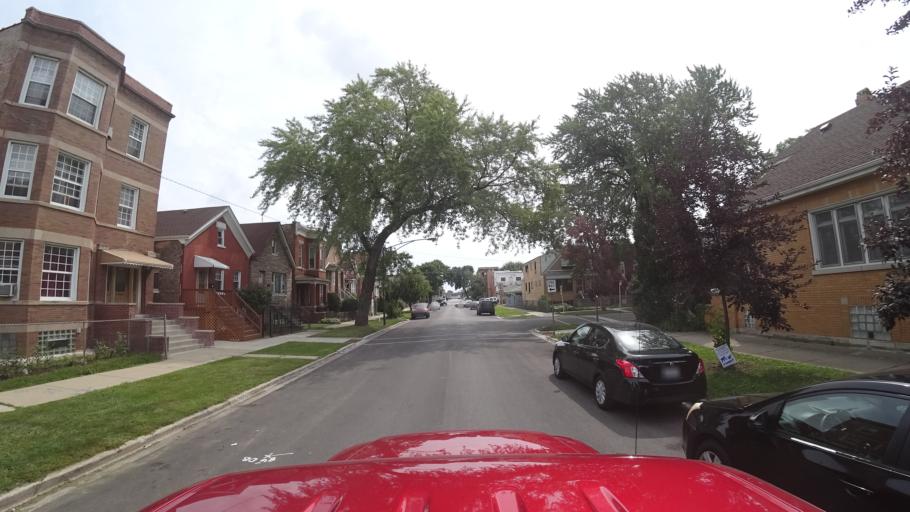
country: US
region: Illinois
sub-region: Cook County
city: Chicago
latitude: 41.8323
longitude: -87.6671
